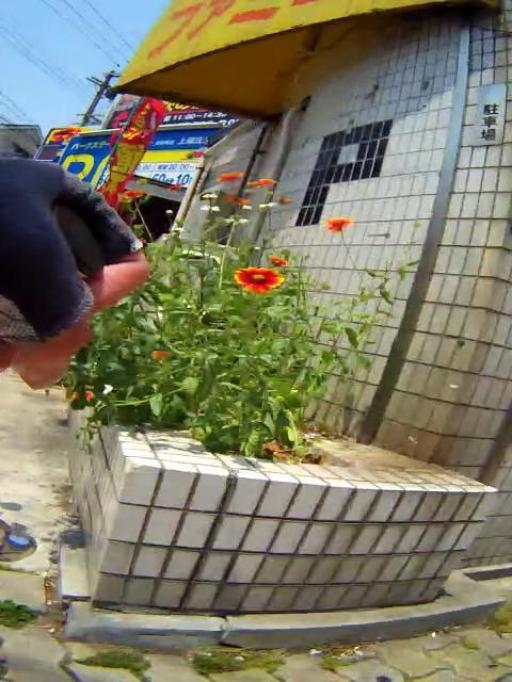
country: JP
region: Osaka
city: Suita
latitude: 34.7489
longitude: 135.5283
